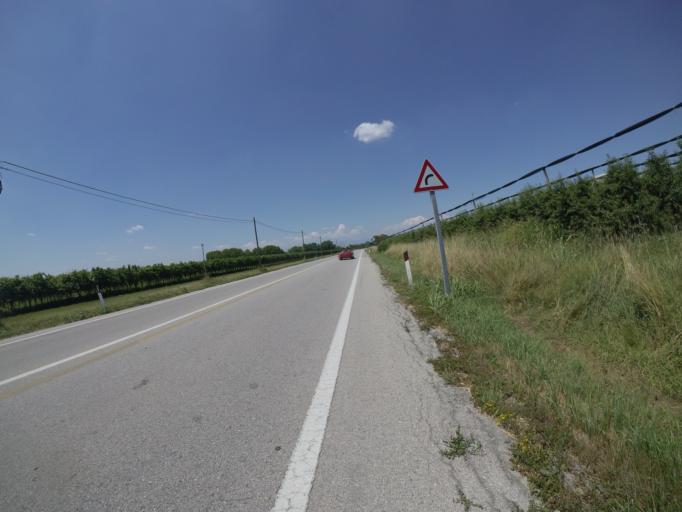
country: IT
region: Friuli Venezia Giulia
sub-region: Provincia di Udine
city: Varmo
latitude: 45.9135
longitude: 12.9992
